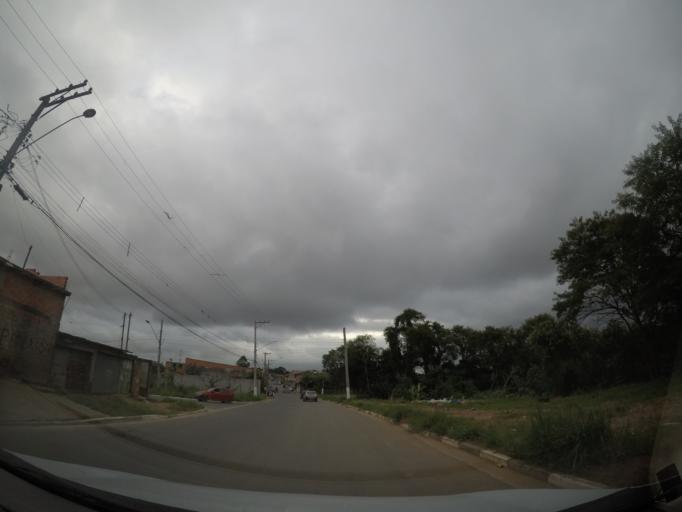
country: BR
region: Sao Paulo
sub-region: Aruja
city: Aruja
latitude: -23.3947
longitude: -46.4200
